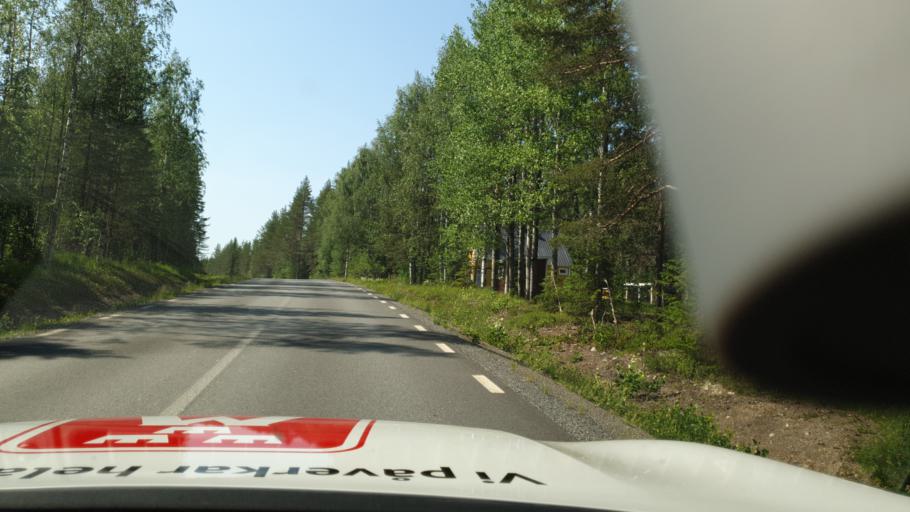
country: SE
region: Vaesterbotten
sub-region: Skelleftea Kommun
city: Langsele
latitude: 64.9759
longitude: 20.0537
